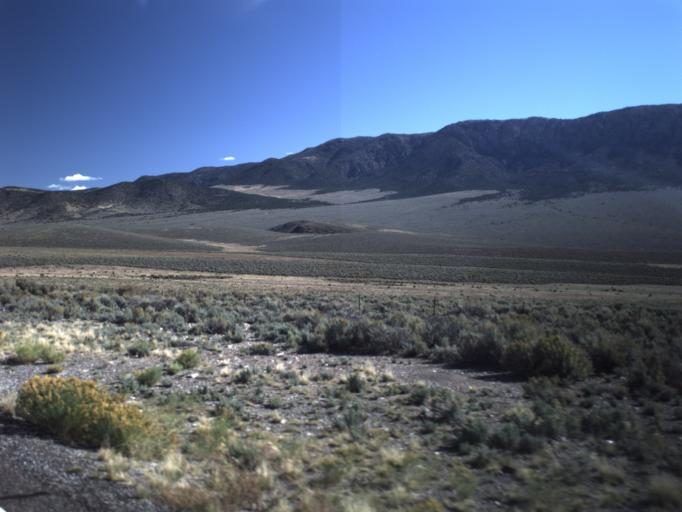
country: US
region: Utah
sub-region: Piute County
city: Junction
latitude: 38.3002
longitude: -111.9715
